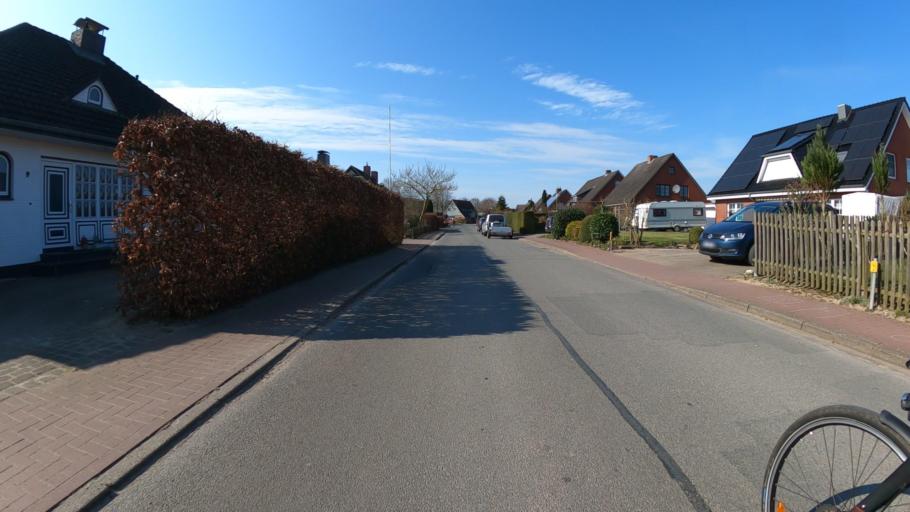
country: DE
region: Schleswig-Holstein
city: Seestermuhe
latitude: 53.7046
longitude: 9.5608
